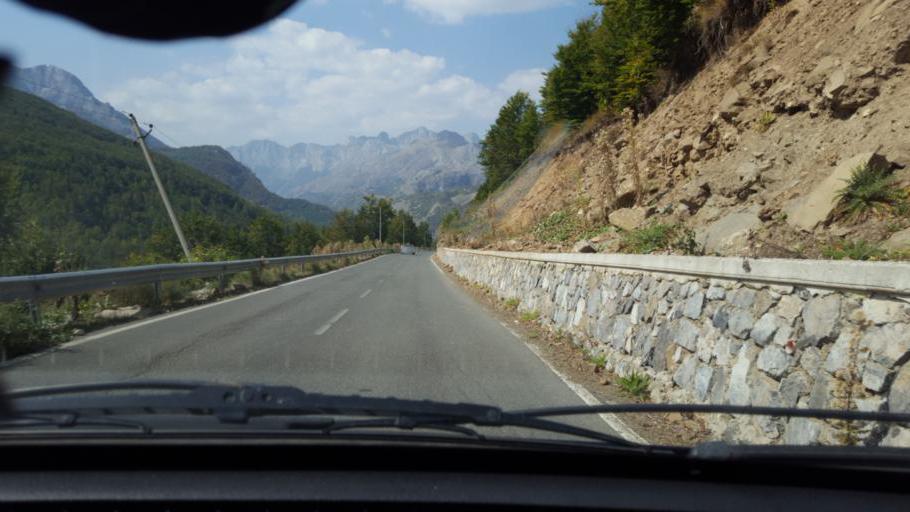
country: AL
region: Kukes
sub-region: Rrethi i Tropojes
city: Valbone
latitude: 42.5346
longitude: 19.7108
